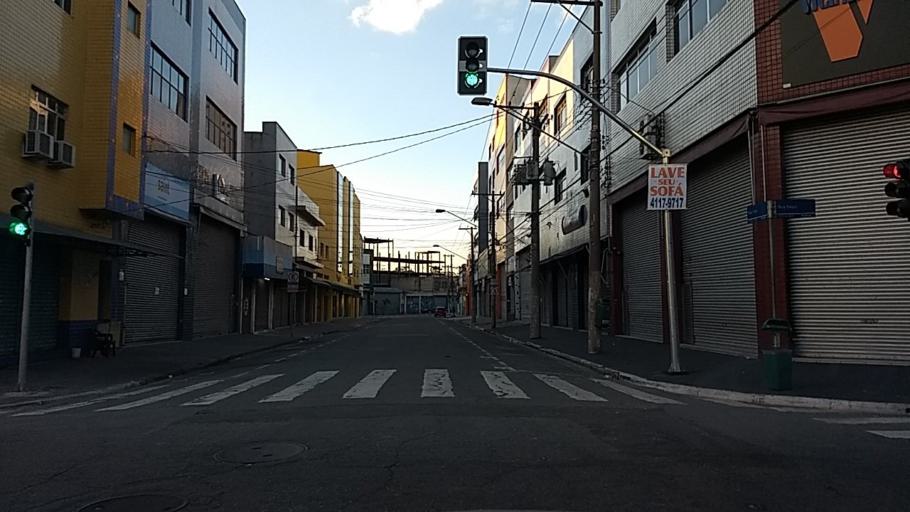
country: BR
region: Sao Paulo
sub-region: Sao Paulo
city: Sao Paulo
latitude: -23.5289
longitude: -46.6196
